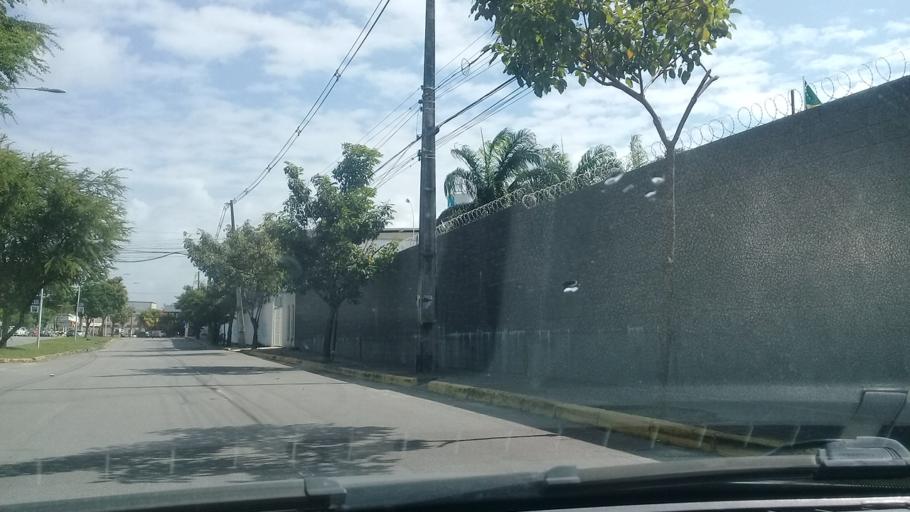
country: BR
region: Pernambuco
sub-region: Jaboatao Dos Guararapes
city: Jaboatao
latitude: -8.1673
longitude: -34.9202
